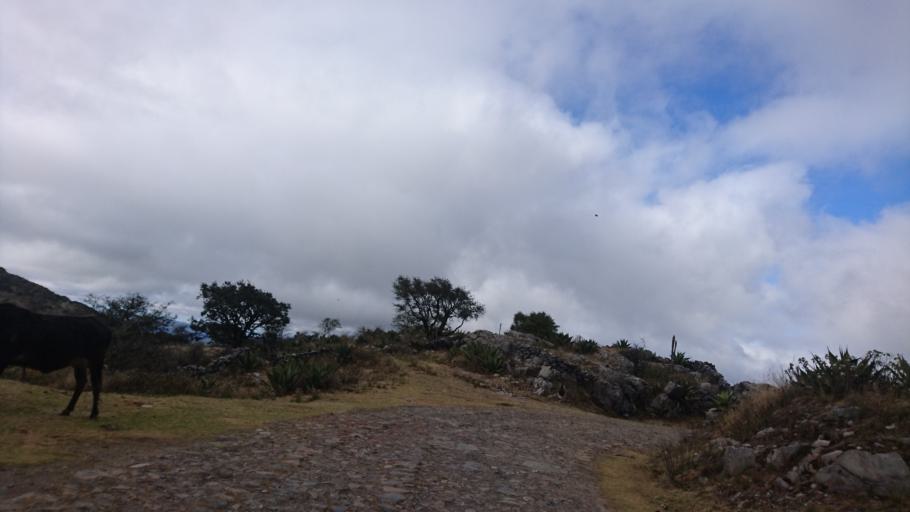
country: MX
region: San Luis Potosi
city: Zaragoza
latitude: 22.0754
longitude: -100.6412
